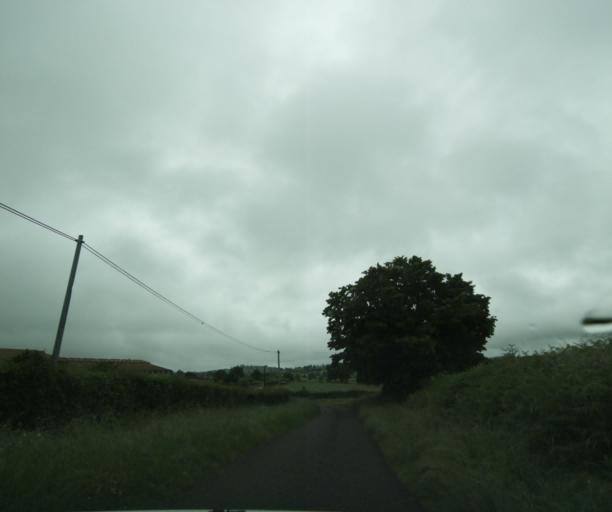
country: FR
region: Bourgogne
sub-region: Departement de Saone-et-Loire
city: La Clayette
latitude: 46.3486
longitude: 4.2311
